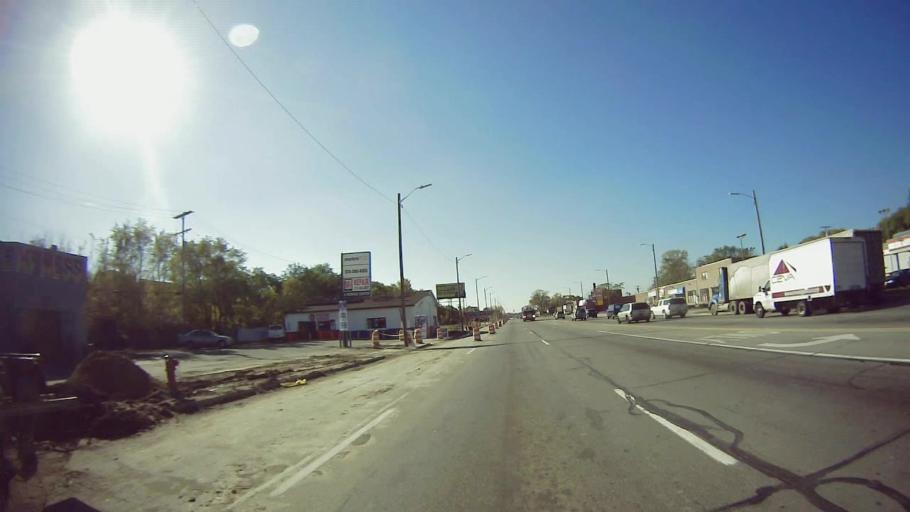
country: US
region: Michigan
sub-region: Wayne County
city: Highland Park
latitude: 42.3908
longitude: -83.1276
